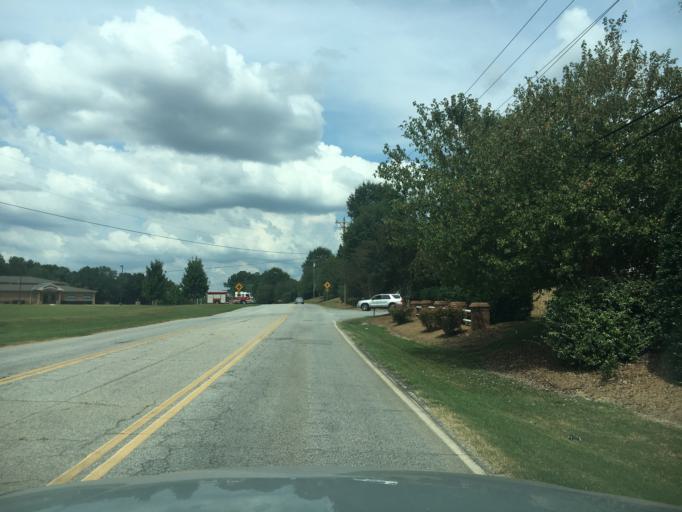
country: US
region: South Carolina
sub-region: Greenville County
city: Five Forks
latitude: 34.8265
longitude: -82.2283
